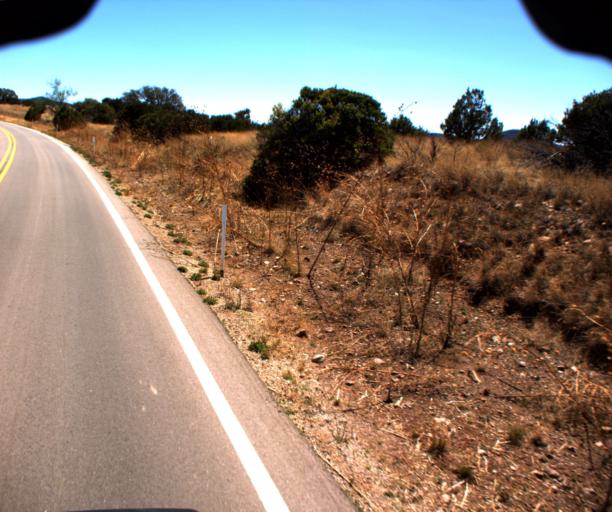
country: US
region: Arizona
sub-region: Cochise County
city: Huachuca City
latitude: 31.5270
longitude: -110.5029
